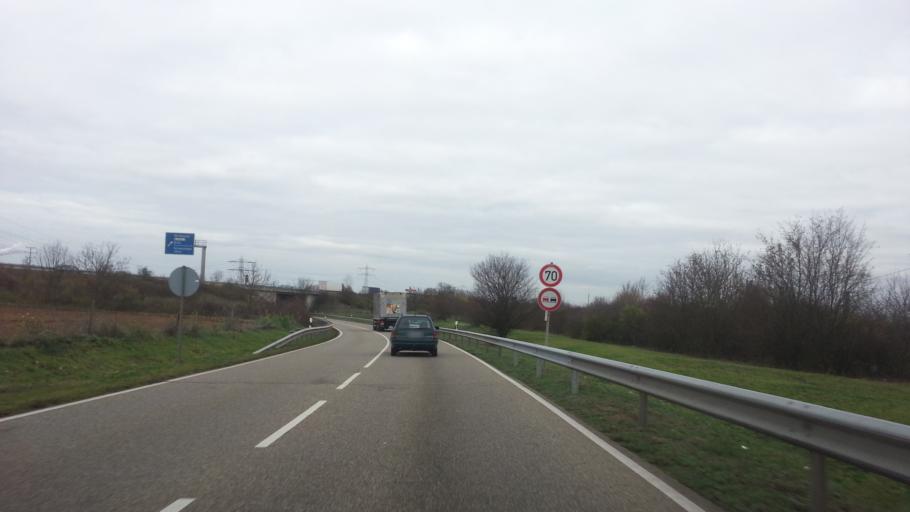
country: DE
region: Baden-Wuerttemberg
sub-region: Karlsruhe Region
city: Bruhl
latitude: 49.4009
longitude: 8.5462
